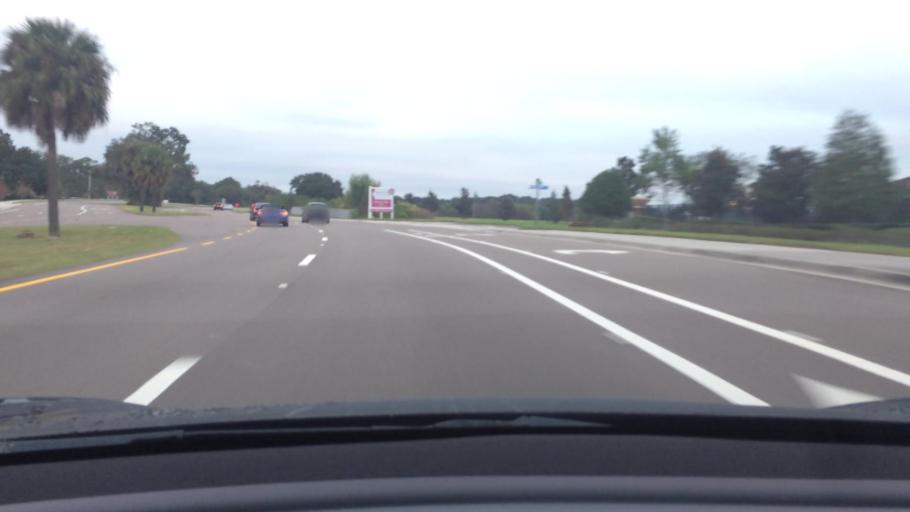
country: US
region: Florida
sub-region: Hillsborough County
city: Progress Village
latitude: 27.8864
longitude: -82.3581
